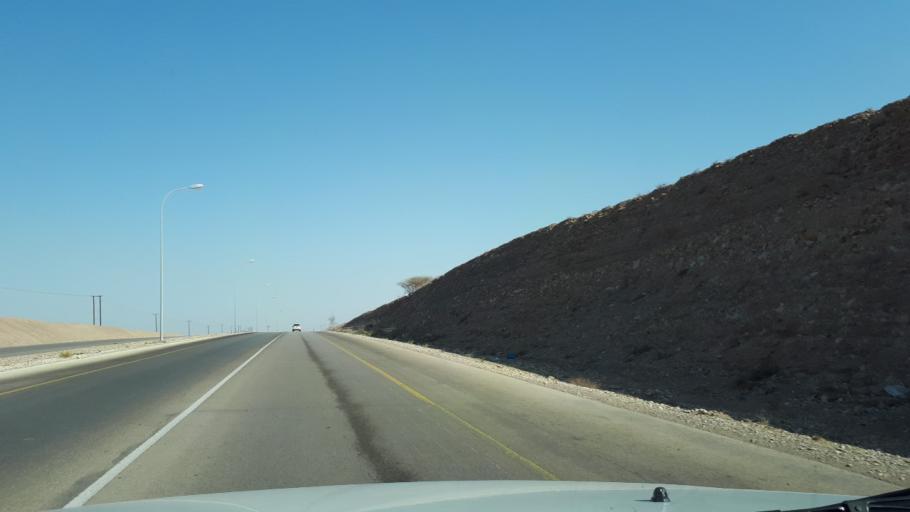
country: OM
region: Ash Sharqiyah
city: Sur
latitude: 22.6346
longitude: 59.4056
